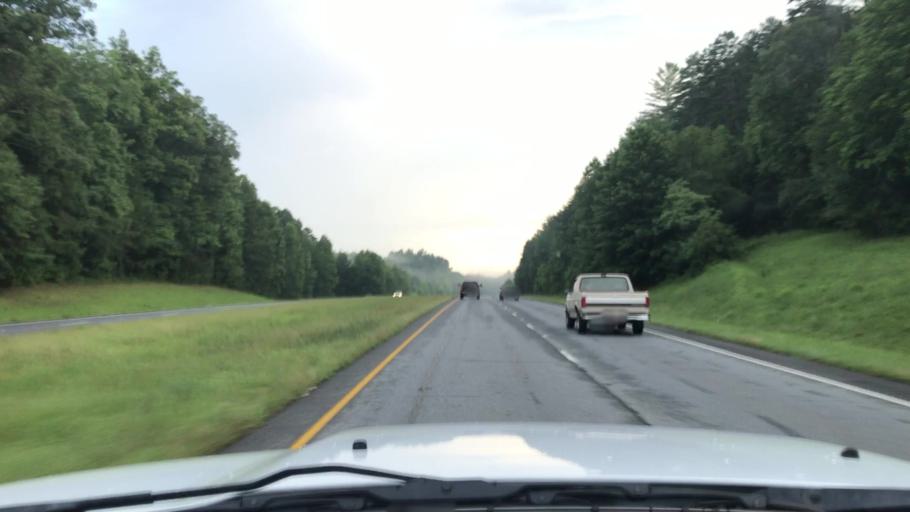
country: US
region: Georgia
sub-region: Fannin County
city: Blue Ridge
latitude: 34.7961
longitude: -84.3808
